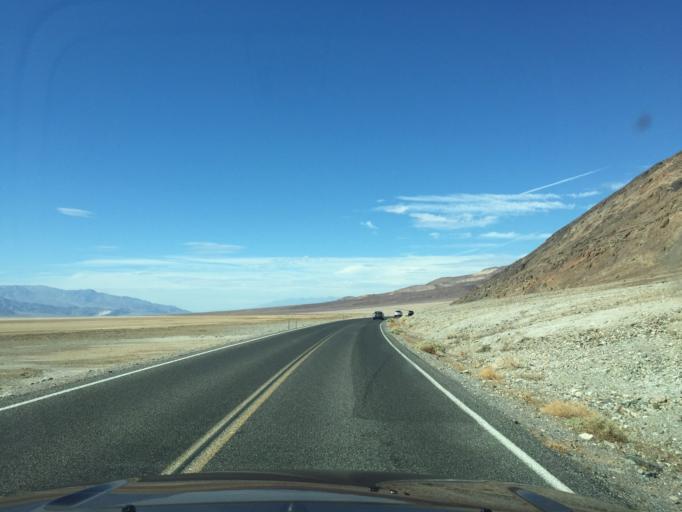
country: US
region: Nevada
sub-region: Nye County
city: Beatty
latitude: 36.2405
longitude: -116.7714
